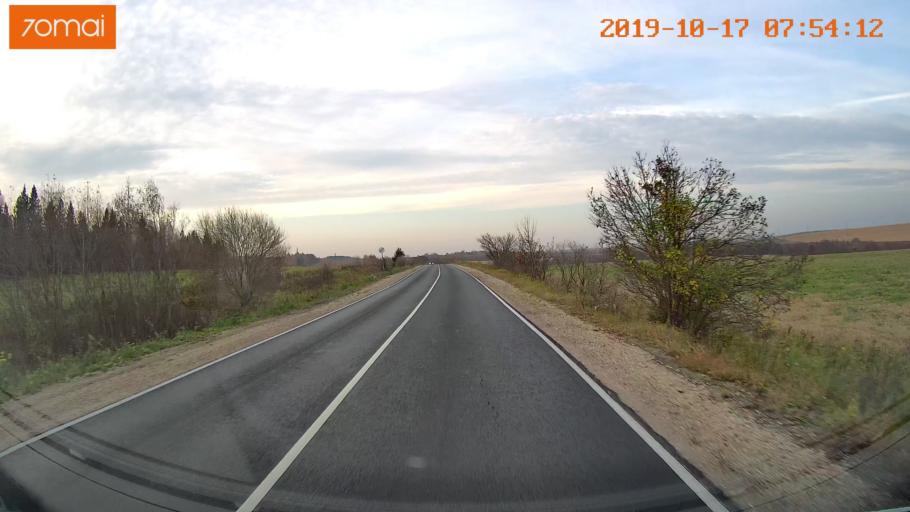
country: RU
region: Vladimir
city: Bavleny
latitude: 56.4520
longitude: 39.6091
